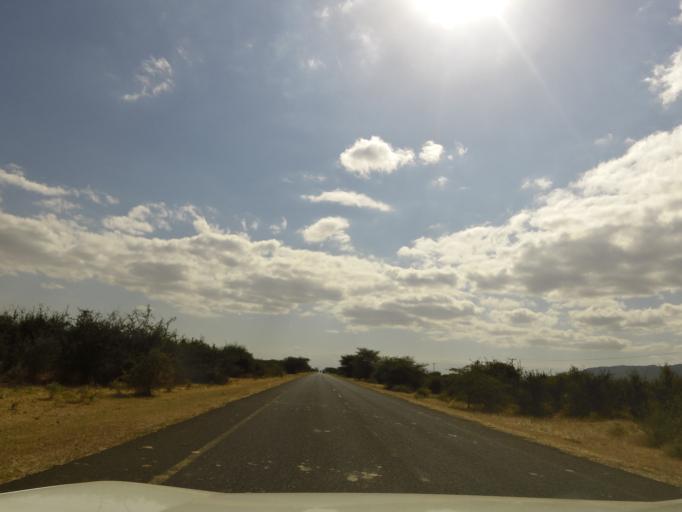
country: TZ
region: Arusha
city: Mto wa Mbu
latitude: -3.5199
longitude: 36.0438
